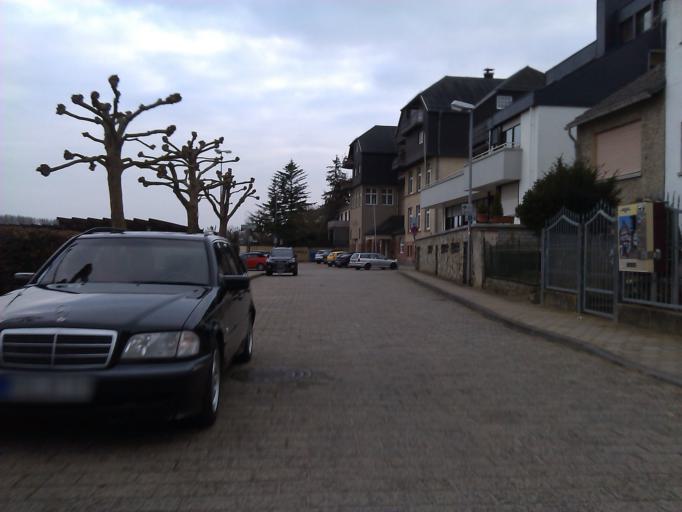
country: DE
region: Rheinland-Pfalz
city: Budenheim
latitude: 50.0346
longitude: 8.1621
